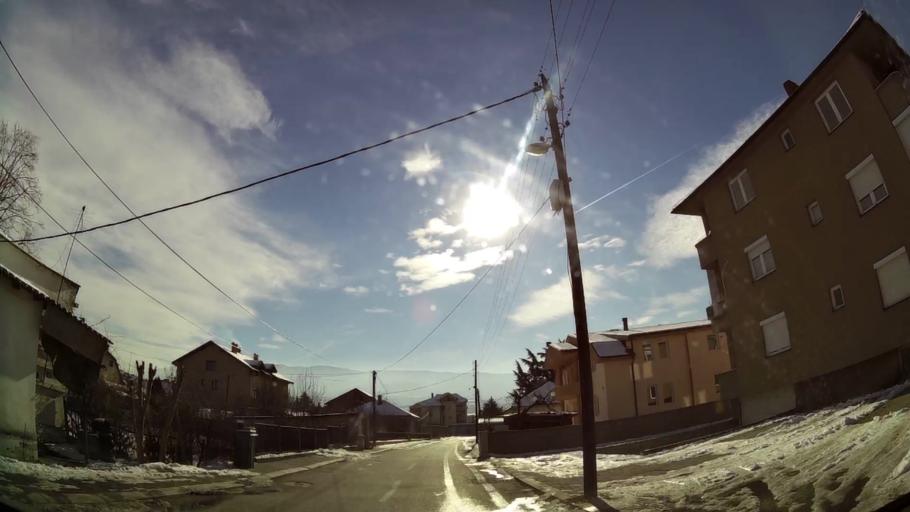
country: MK
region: Saraj
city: Saraj
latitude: 42.0104
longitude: 21.3574
